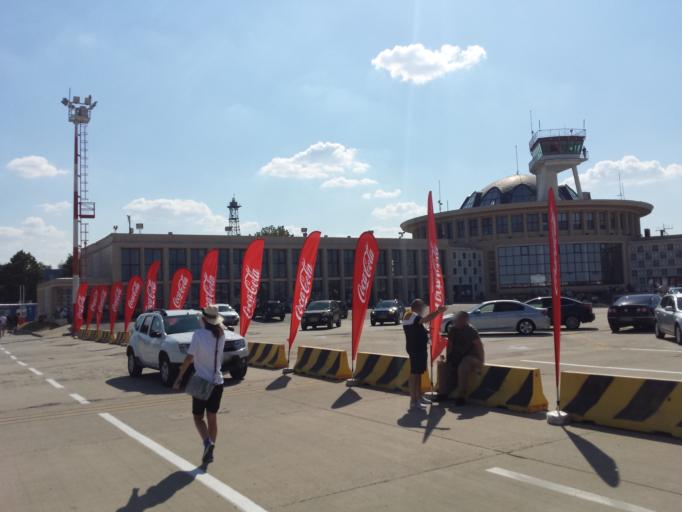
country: RO
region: Ilfov
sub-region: Comuna Otopeni
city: Otopeni
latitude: 44.4966
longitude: 26.0826
